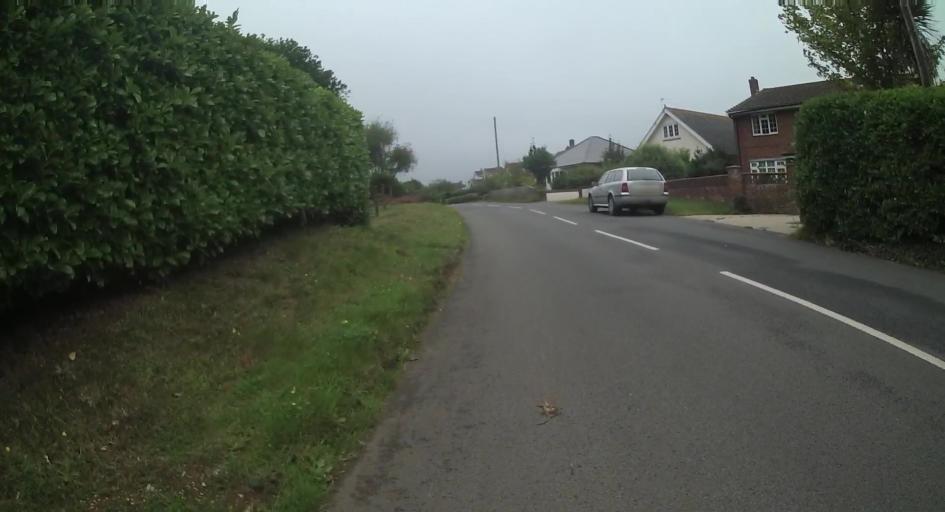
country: GB
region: England
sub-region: Isle of Wight
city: Newchurch
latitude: 50.6566
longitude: -1.1996
